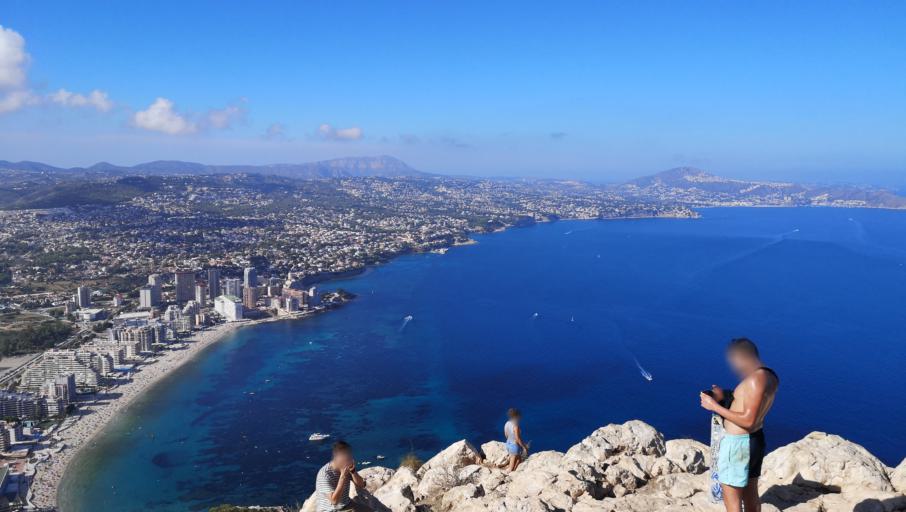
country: ES
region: Valencia
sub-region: Provincia de Alicante
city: Calp
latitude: 38.6350
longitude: 0.0745
